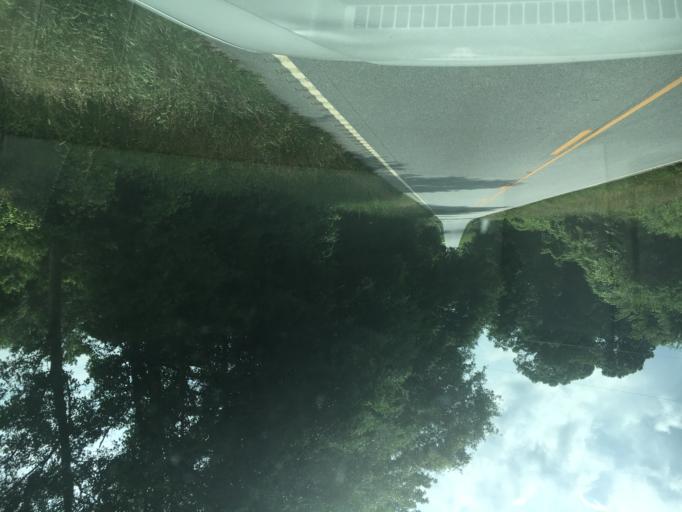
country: US
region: South Carolina
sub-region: Laurens County
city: Watts Mills
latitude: 34.5316
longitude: -81.9680
